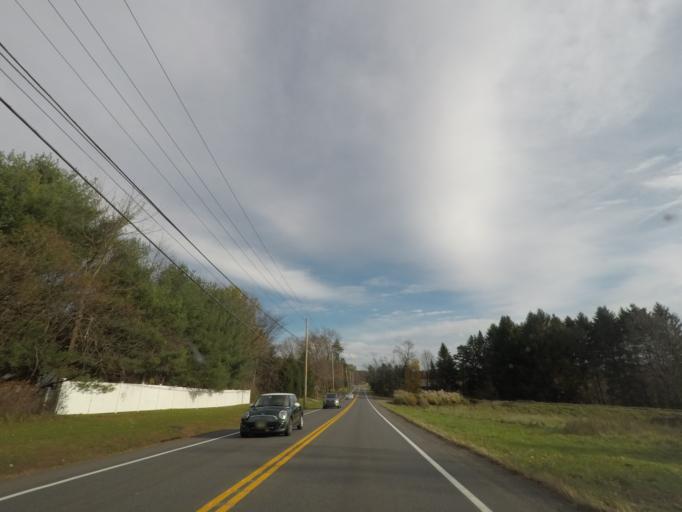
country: US
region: New York
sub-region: Albany County
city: Voorheesville
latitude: 42.6459
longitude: -73.9112
